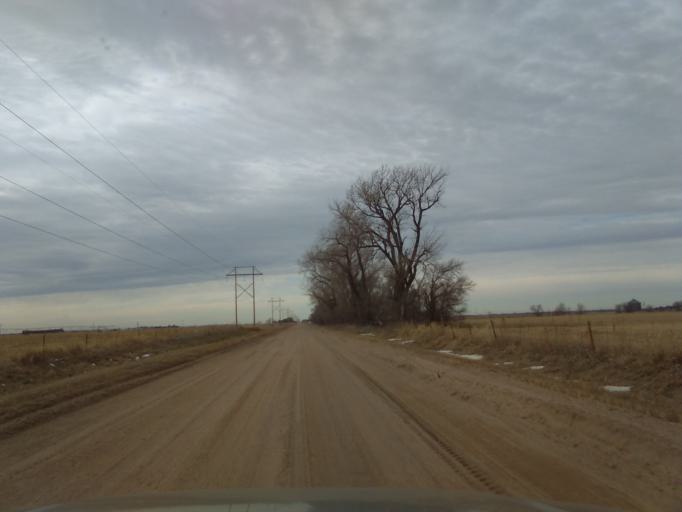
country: US
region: Nebraska
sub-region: Buffalo County
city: Shelton
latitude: 40.6548
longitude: -98.7554
